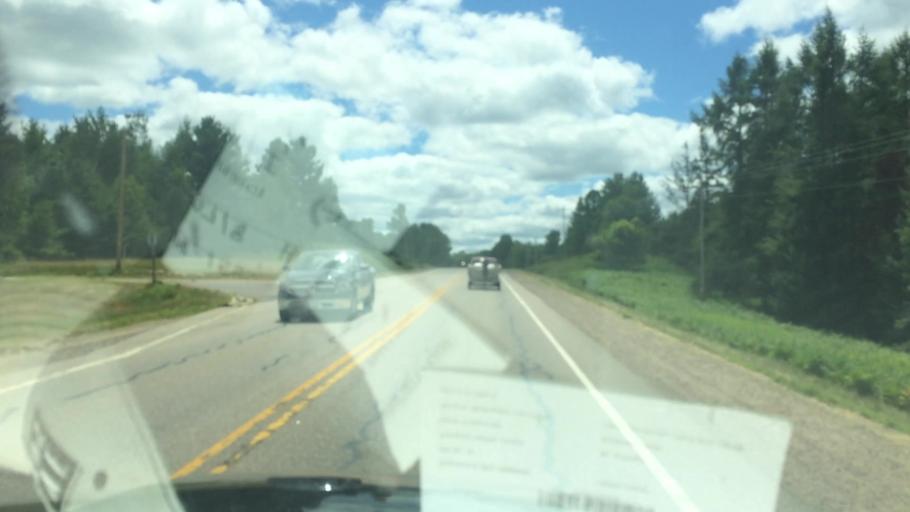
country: US
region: Wisconsin
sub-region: Vilas County
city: Eagle River
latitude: 45.7966
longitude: -89.3204
